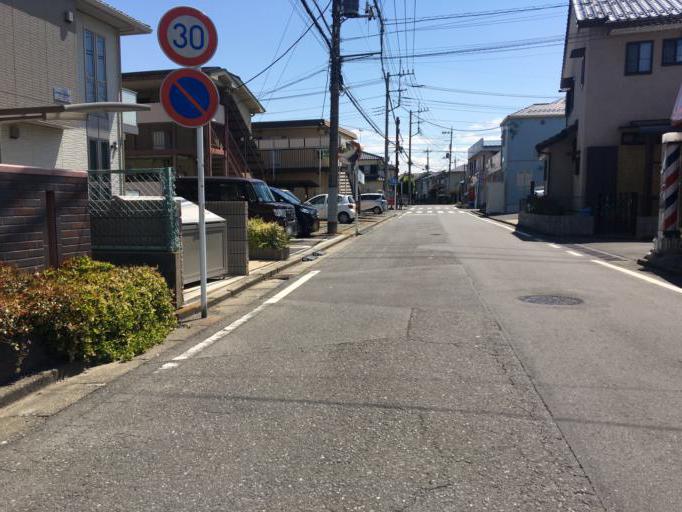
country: JP
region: Saitama
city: Kawagoe
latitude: 35.9264
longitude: 139.4468
